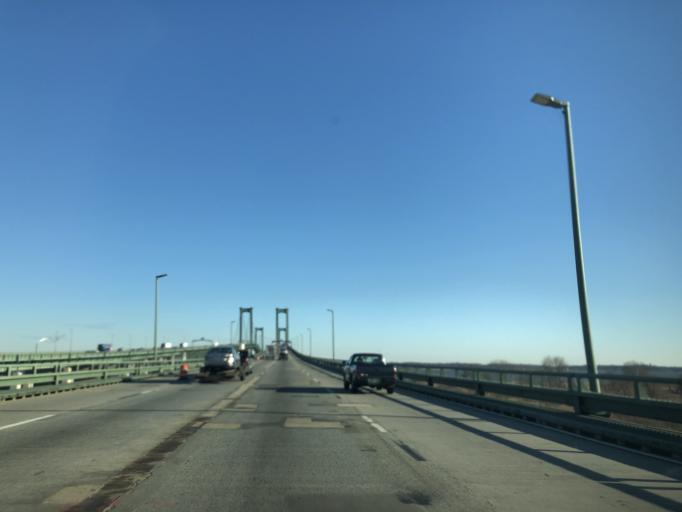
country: US
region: New Jersey
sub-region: Salem County
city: Pennsville
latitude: 39.6936
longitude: -75.5351
